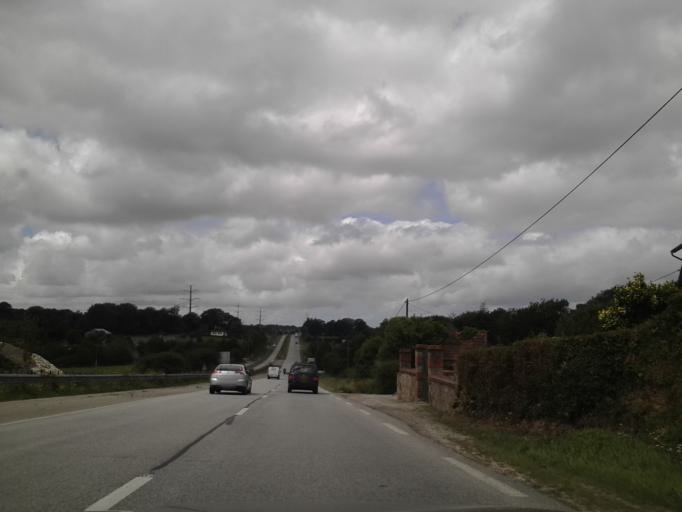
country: FR
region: Lower Normandy
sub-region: Departement de la Manche
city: La Glacerie
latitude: 49.5777
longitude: -1.5817
